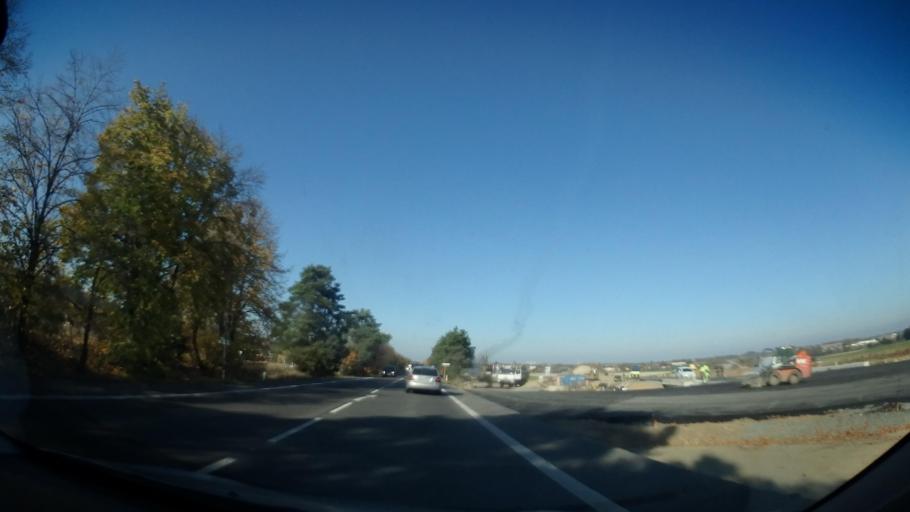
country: CZ
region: Pardubicky
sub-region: Okres Chrudim
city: Slatinany
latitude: 49.9069
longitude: 15.8208
